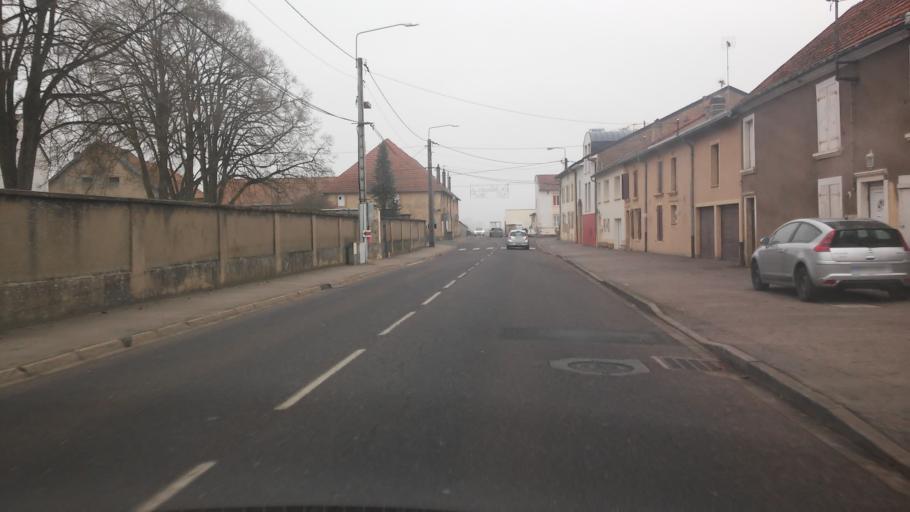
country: FR
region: Lorraine
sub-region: Departement de la Moselle
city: Augny
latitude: 49.0585
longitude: 6.1221
